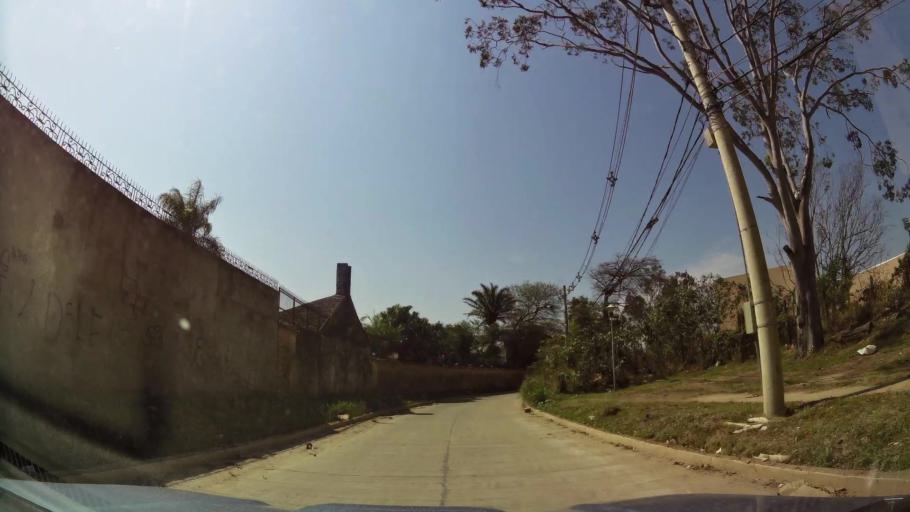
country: BO
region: Santa Cruz
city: Santa Cruz de la Sierra
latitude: -17.7482
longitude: -63.1770
